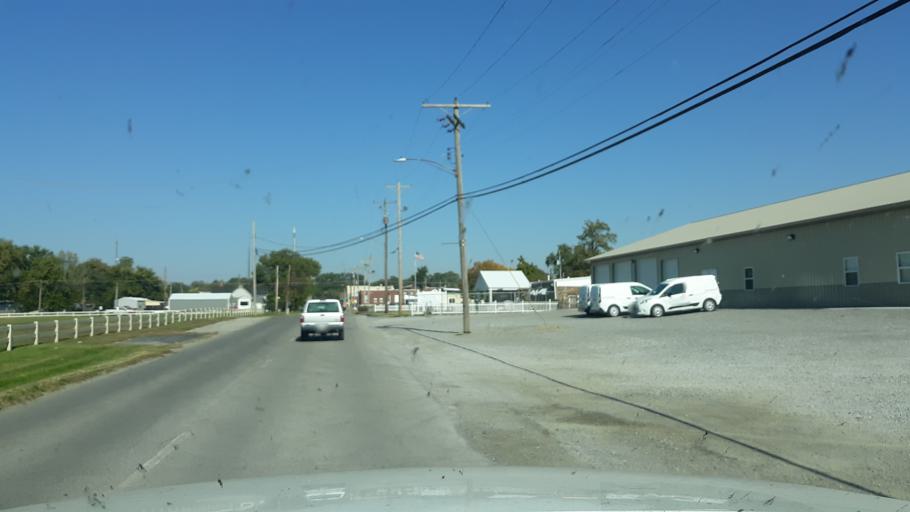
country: US
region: Illinois
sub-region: Saline County
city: Eldorado
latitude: 37.8105
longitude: -88.4358
